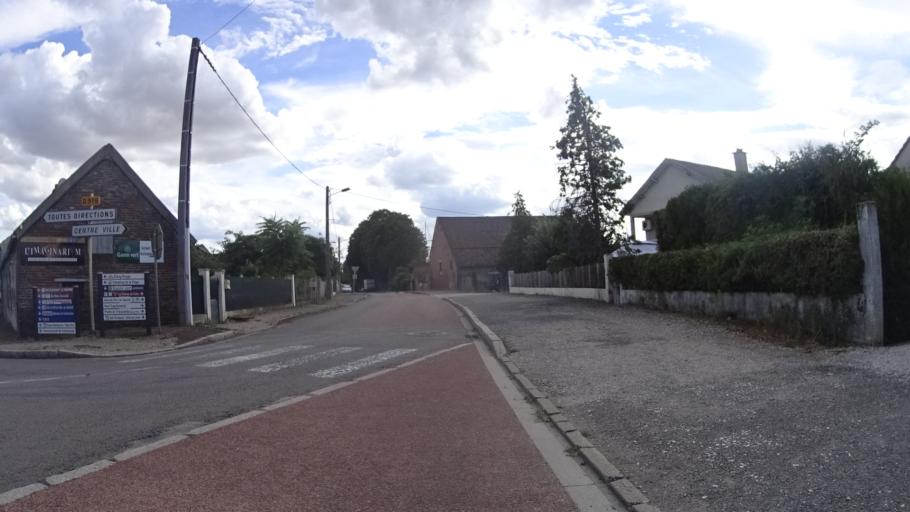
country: FR
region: Bourgogne
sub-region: Departement de la Cote-d'Or
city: Seurre
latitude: 47.0042
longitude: 5.1502
